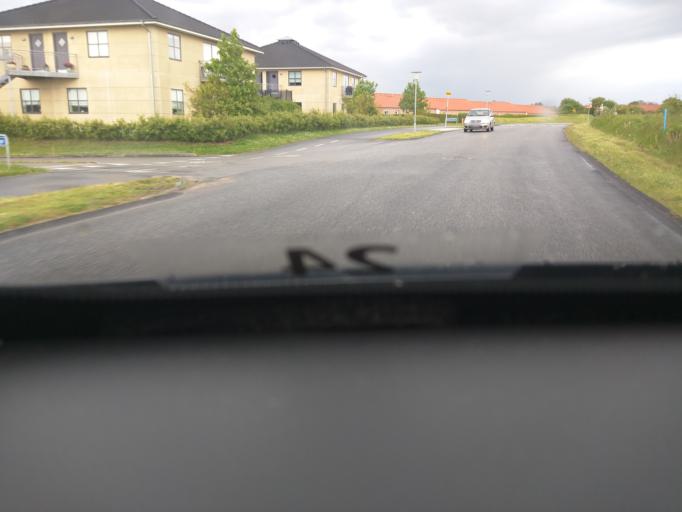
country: DK
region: Central Jutland
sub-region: Viborg Kommune
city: Viborg
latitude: 56.4502
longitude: 9.4533
